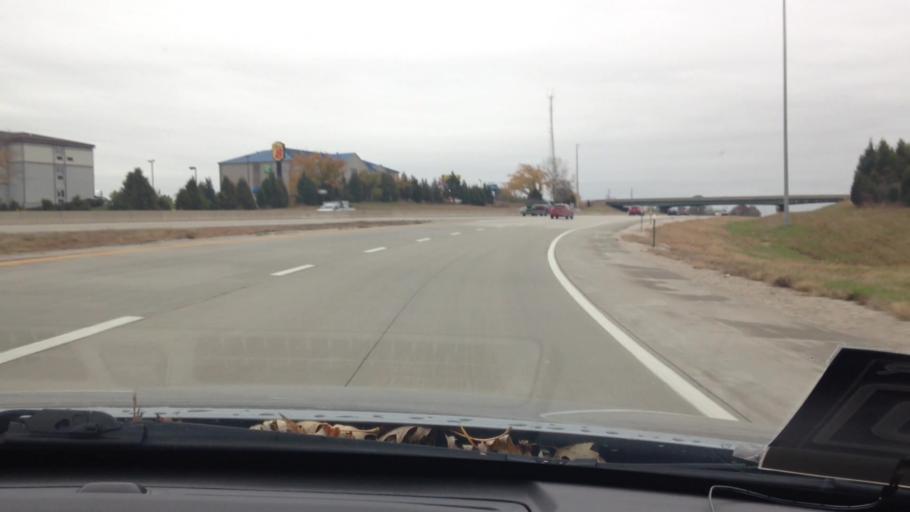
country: US
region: Kansas
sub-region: Wyandotte County
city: Bonner Springs
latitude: 39.0957
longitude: -94.8856
